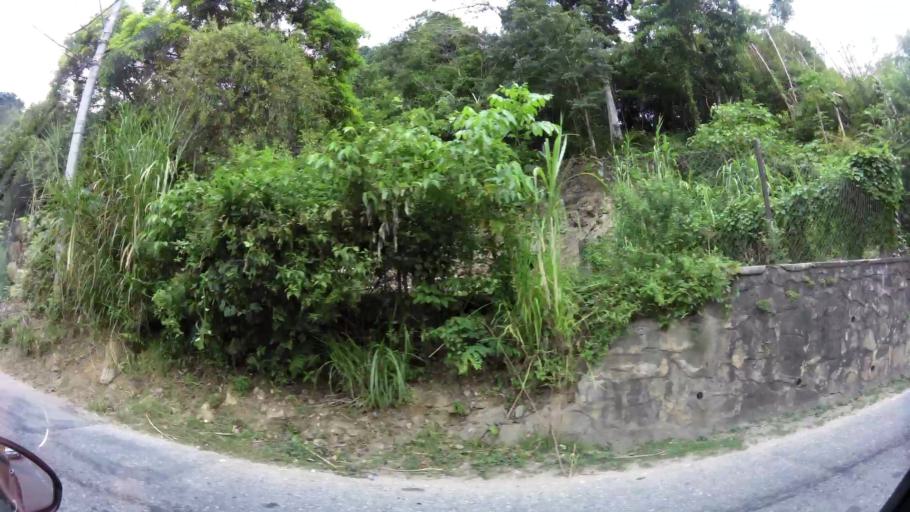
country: TT
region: Diego Martin
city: Petit Valley
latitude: 10.7163
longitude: -61.4737
